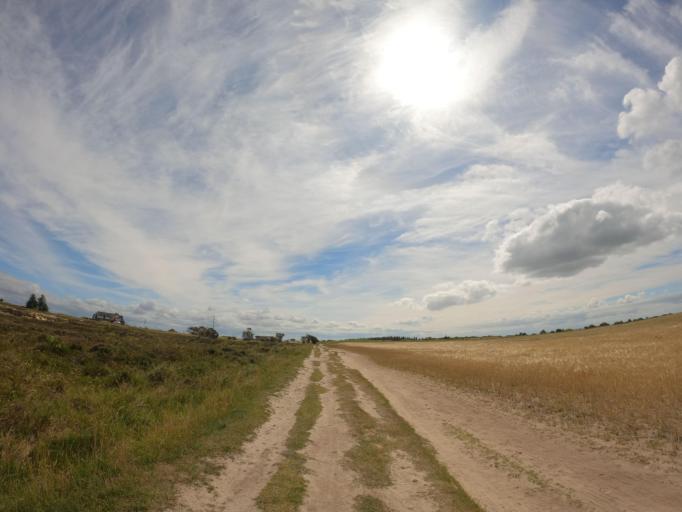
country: DE
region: Schleswig-Holstein
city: Sylt-Ost
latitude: 54.8733
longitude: 8.4550
